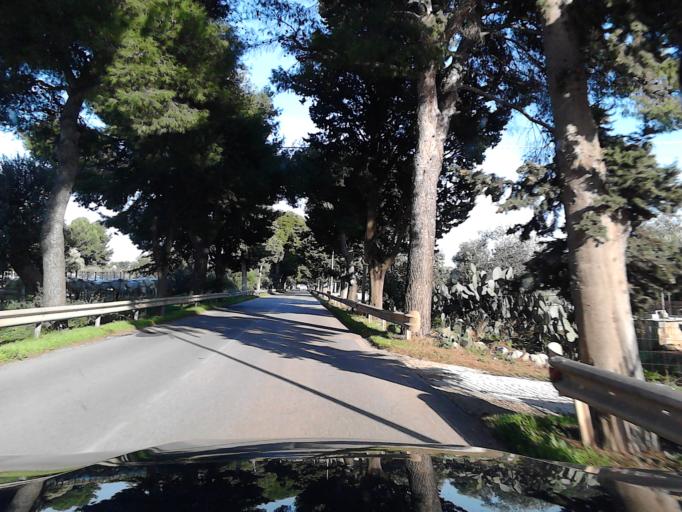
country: IT
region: Apulia
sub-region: Provincia di Bari
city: Mola di Bari
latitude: 41.0464
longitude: 17.0666
